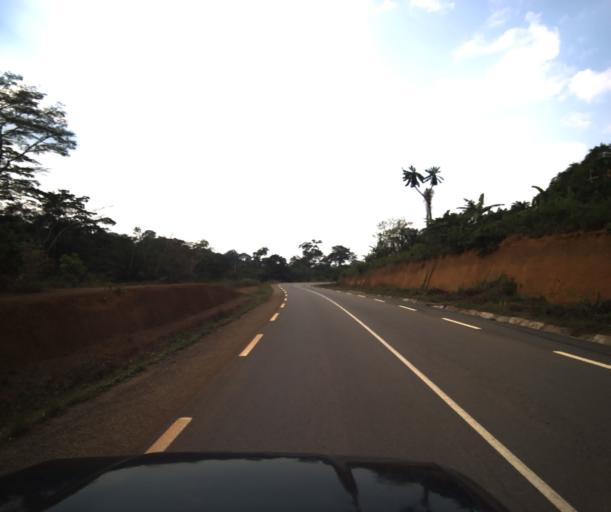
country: CM
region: Centre
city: Mbankomo
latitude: 3.6584
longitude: 11.3412
